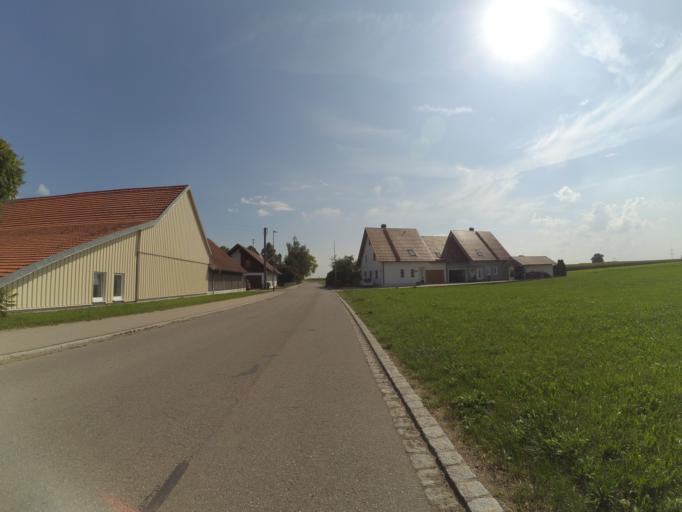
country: DE
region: Bavaria
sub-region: Swabia
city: Lamerdingen
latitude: 48.1029
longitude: 10.7703
